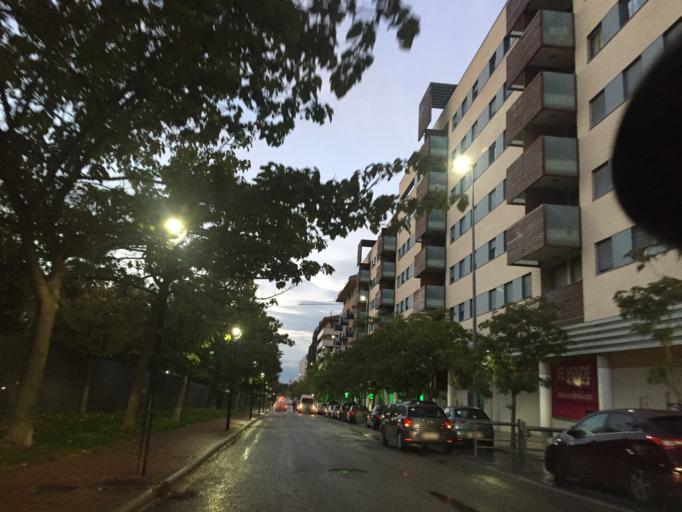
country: ES
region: Andalusia
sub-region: Provincia de Jaen
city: Jaen
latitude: 37.7868
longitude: -3.7900
